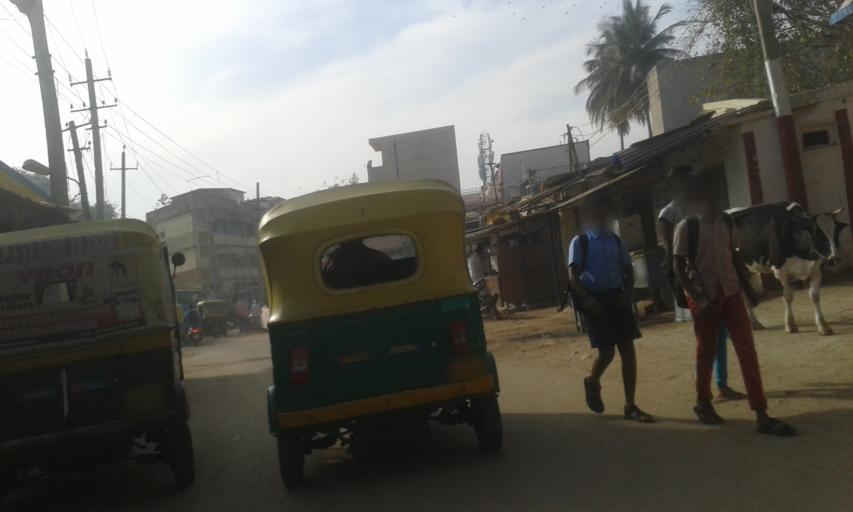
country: IN
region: Karnataka
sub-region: Bangalore Urban
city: Bangalore
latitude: 12.9579
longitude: 77.6188
